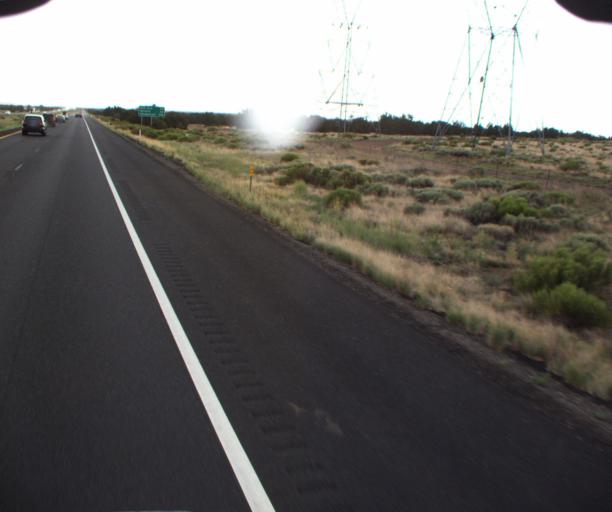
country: US
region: Arizona
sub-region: Coconino County
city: Flagstaff
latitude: 35.1963
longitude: -111.3940
